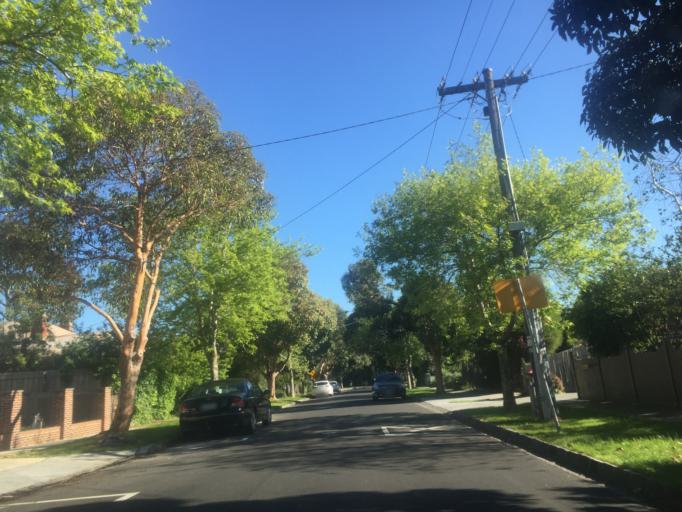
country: AU
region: Victoria
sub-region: Boroondara
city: Canterbury
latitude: -37.8160
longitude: 145.0859
